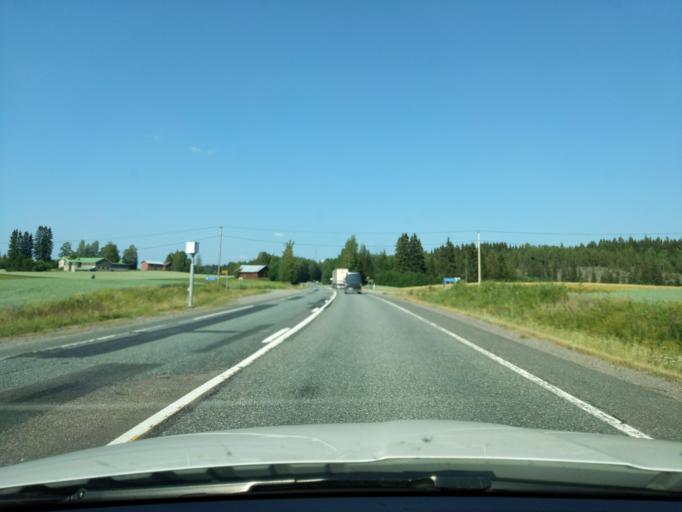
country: FI
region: Paijanne Tavastia
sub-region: Lahti
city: Hollola
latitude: 60.9671
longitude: 25.4644
